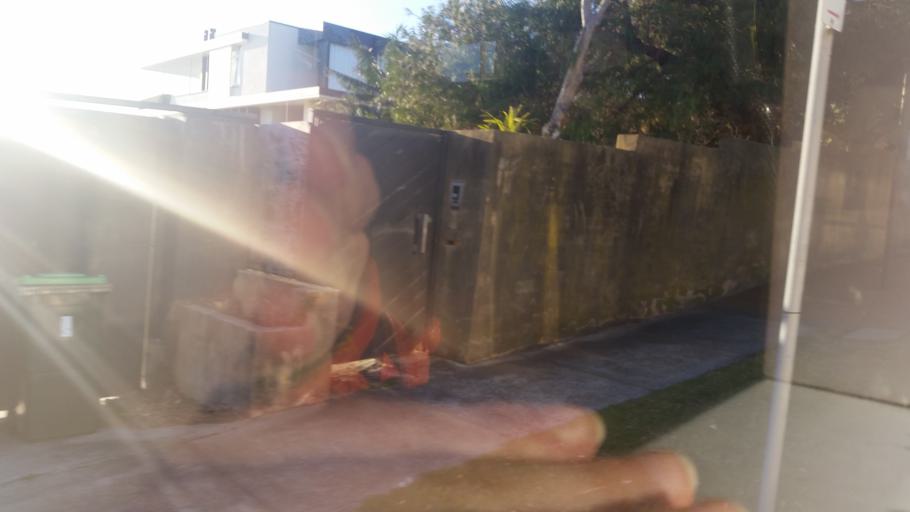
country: AU
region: New South Wales
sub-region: Waverley
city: Bronte
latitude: -33.9062
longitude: 151.2690
